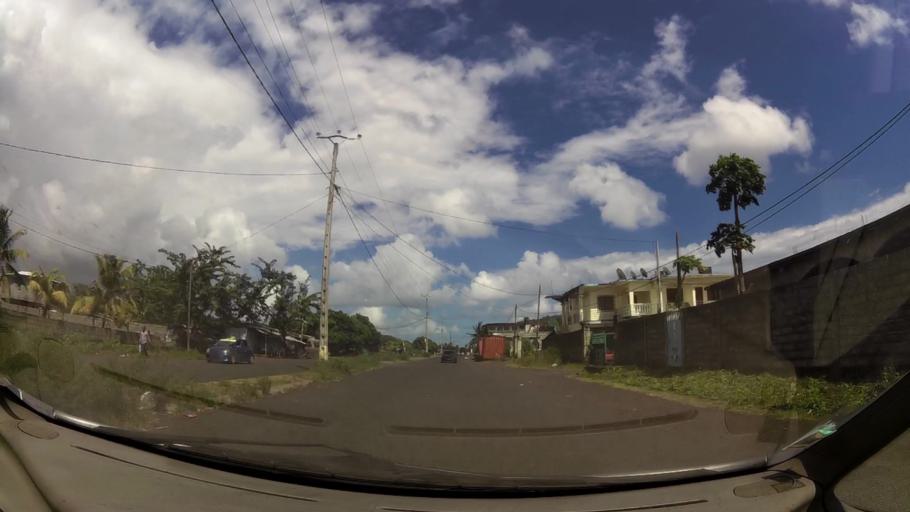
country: KM
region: Grande Comore
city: Mavingouni
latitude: -11.7267
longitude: 43.2443
